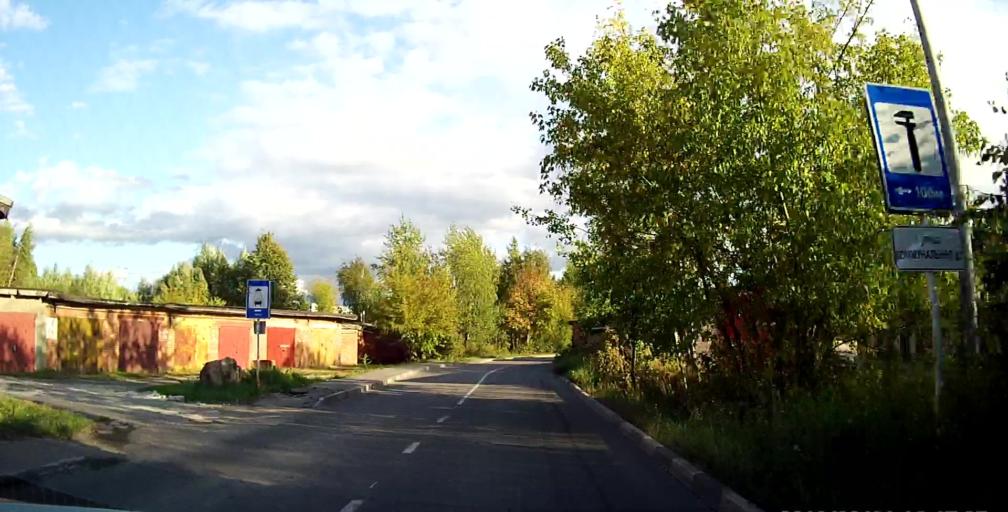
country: RU
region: Moskovskaya
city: Klimovsk
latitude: 55.3649
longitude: 37.5498
